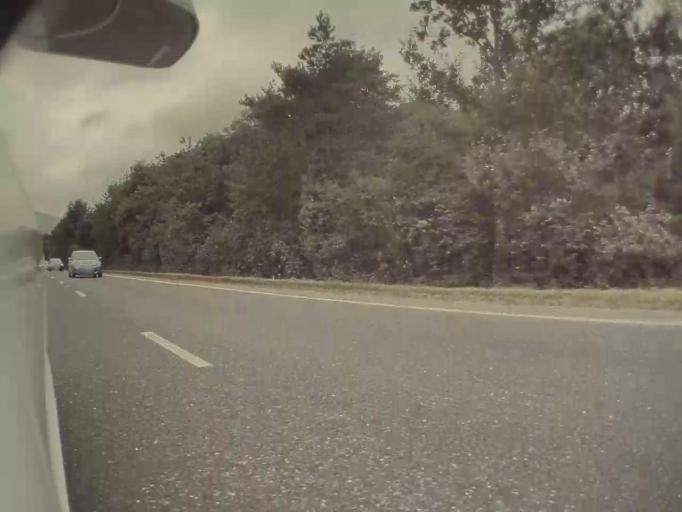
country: GB
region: Wales
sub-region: Conwy
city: Llanfairfechan
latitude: 53.2505
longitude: -3.9928
